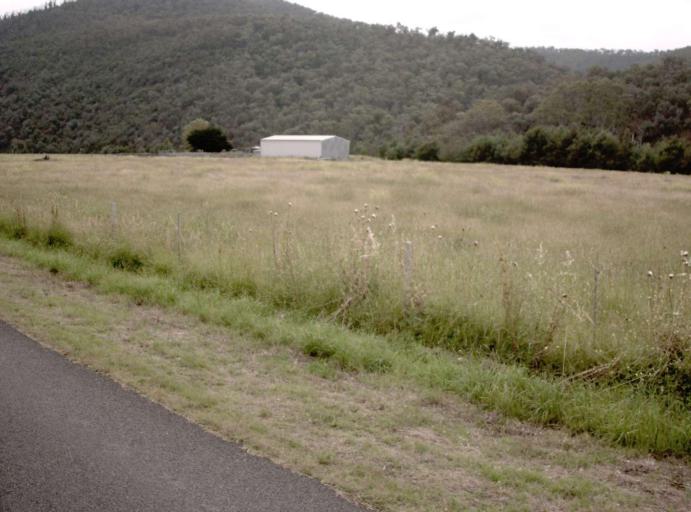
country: AU
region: Victoria
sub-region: Wellington
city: Heyfield
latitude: -37.7963
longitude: 146.6757
